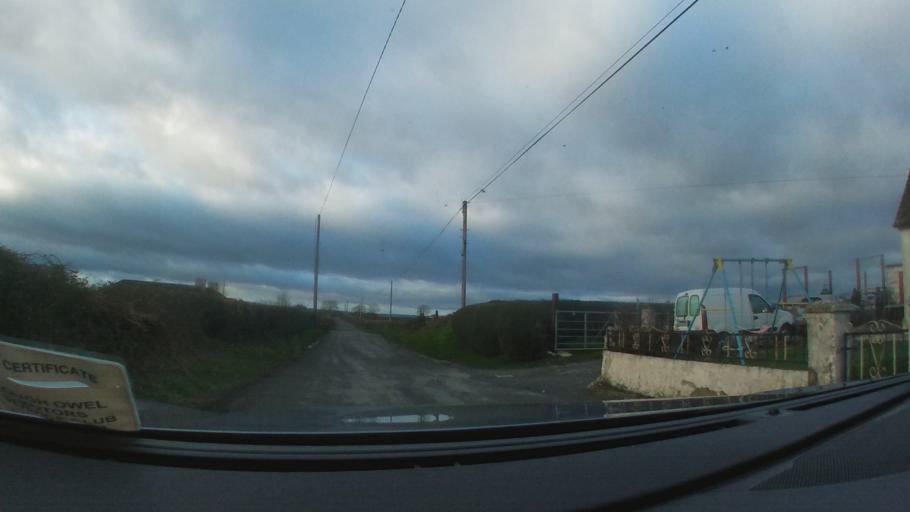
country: IE
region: Leinster
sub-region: Kilkenny
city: Thomastown
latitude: 52.5777
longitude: -7.1569
